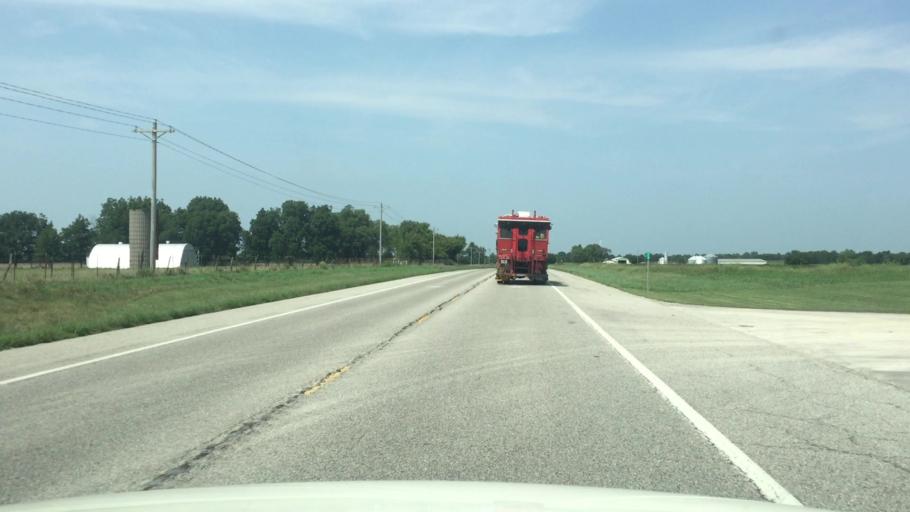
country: US
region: Missouri
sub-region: Jasper County
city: Carl Junction
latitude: 37.2312
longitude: -94.7049
